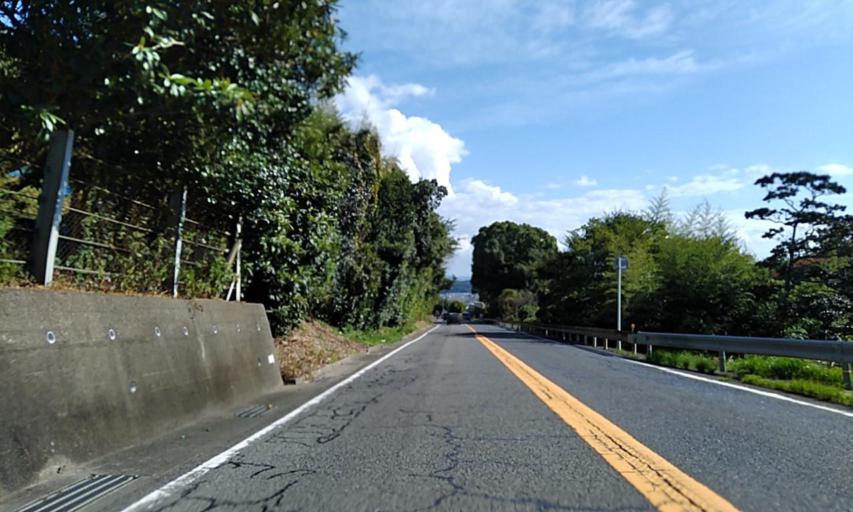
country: JP
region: Wakayama
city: Tanabe
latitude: 33.7803
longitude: 135.3046
